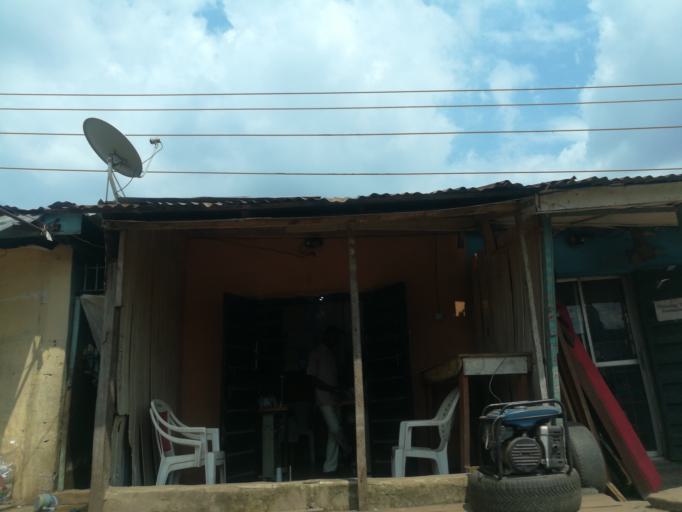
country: NG
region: Oyo
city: Ibadan
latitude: 7.4002
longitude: 3.8855
